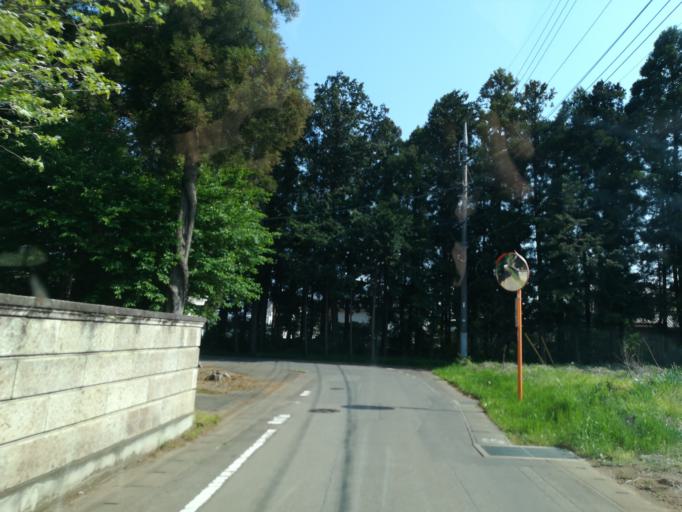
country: JP
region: Ibaraki
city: Tsukuba
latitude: 36.1131
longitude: 140.0787
